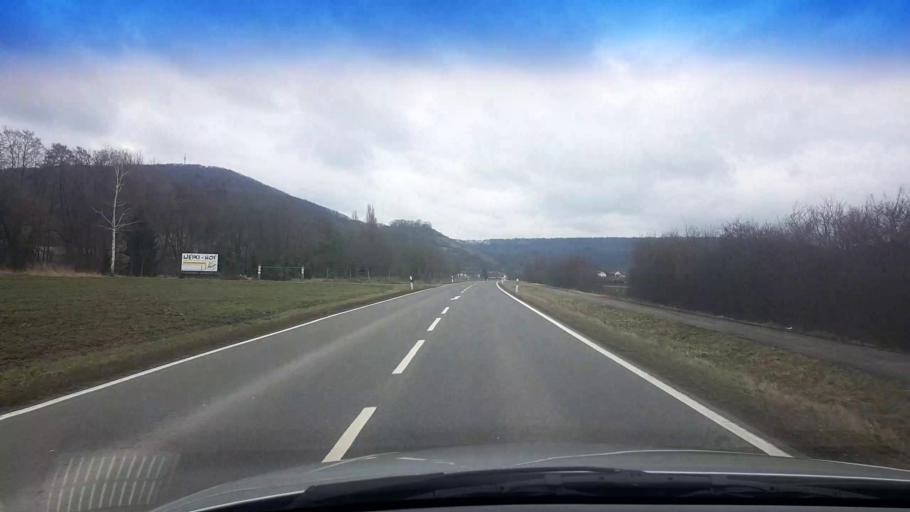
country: DE
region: Bavaria
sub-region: Regierungsbezirk Unterfranken
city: Knetzgau
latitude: 49.9764
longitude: 10.5594
